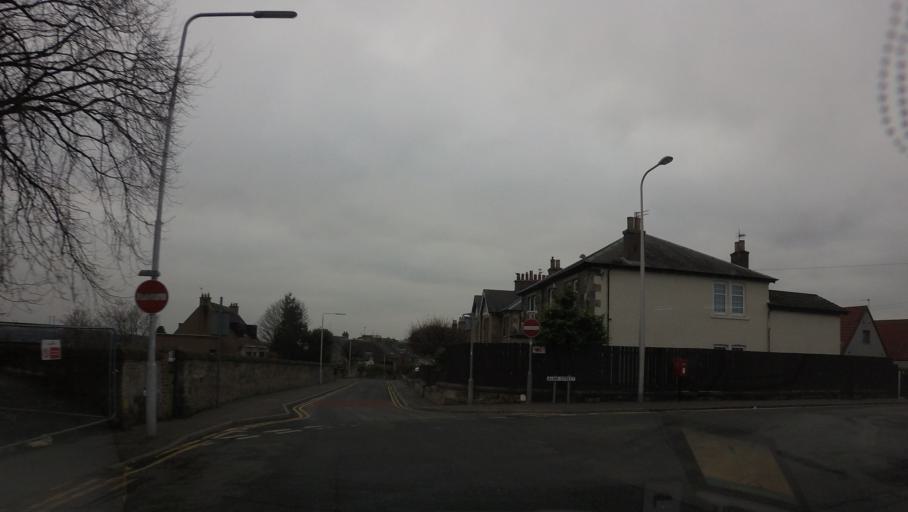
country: GB
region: Scotland
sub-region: Fife
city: Inverkeithing
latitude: 56.0326
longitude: -3.3908
